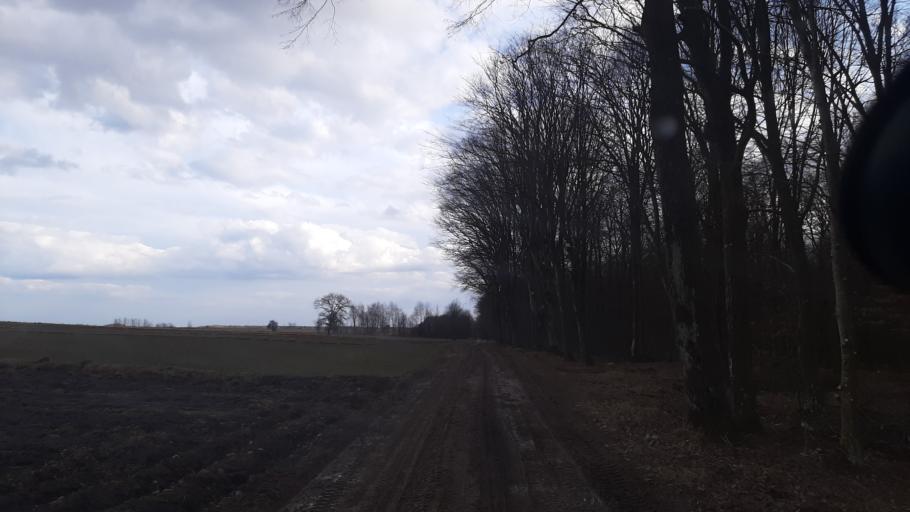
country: PL
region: Lublin Voivodeship
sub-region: Powiat lubelski
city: Jastkow
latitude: 51.3733
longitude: 22.4153
